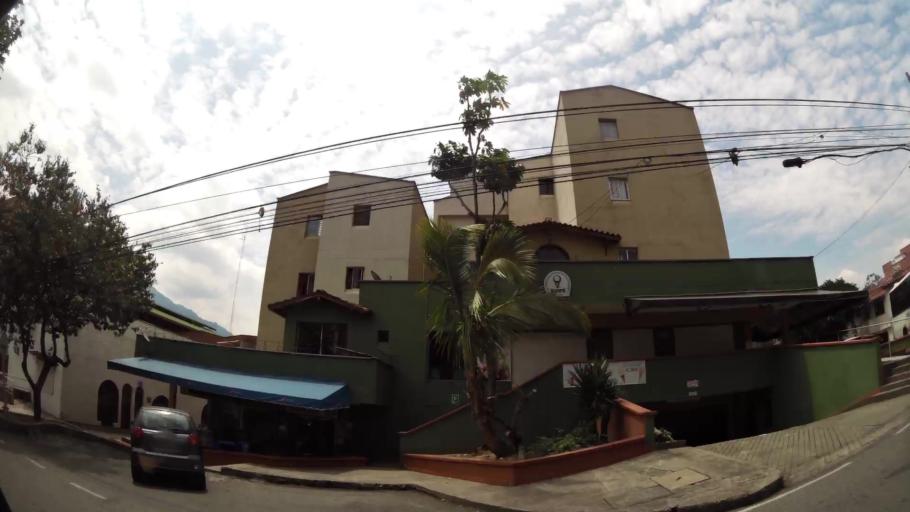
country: CO
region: Antioquia
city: Bello
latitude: 6.3139
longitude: -75.5596
